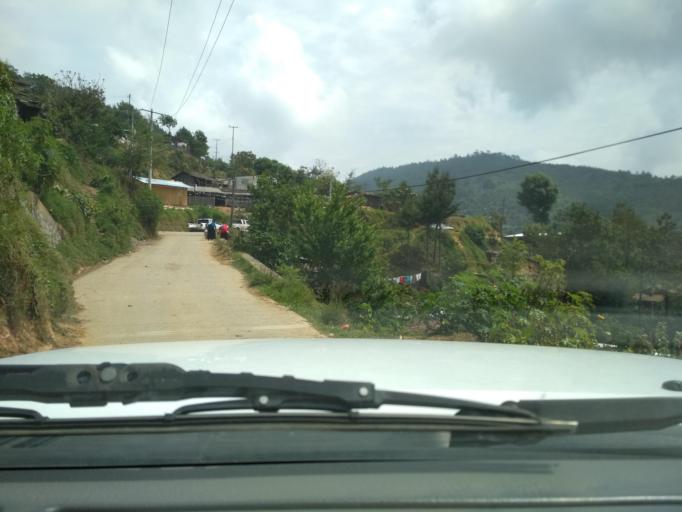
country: MX
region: Veracruz
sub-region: Camerino Z. Mendoza
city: Necoxtla
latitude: 18.7789
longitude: -97.1552
